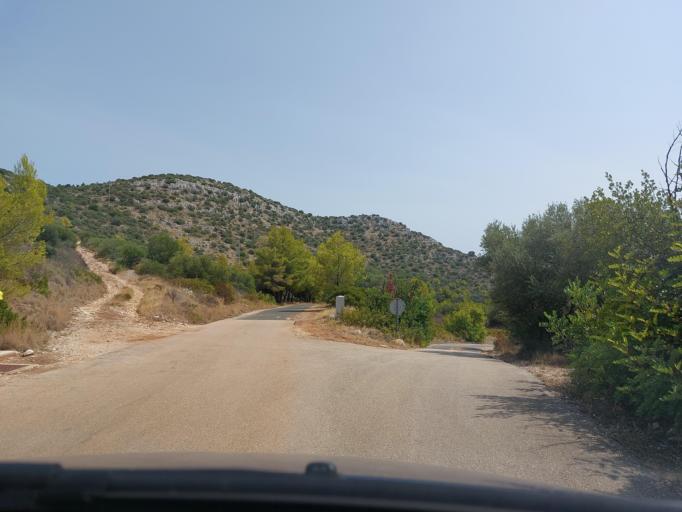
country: HR
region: Dubrovacko-Neretvanska
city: Smokvica
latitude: 42.7394
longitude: 16.8873
